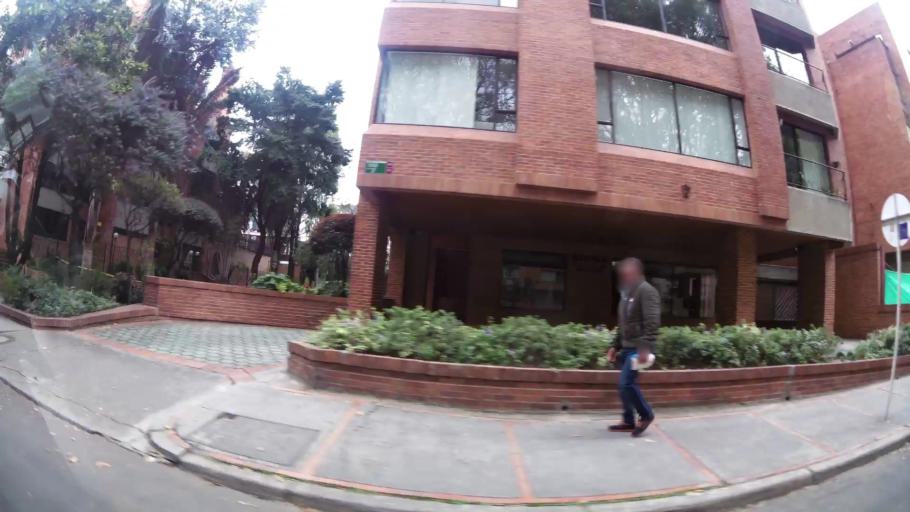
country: CO
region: Bogota D.C.
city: Barrio San Luis
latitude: 4.6743
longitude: -74.0491
